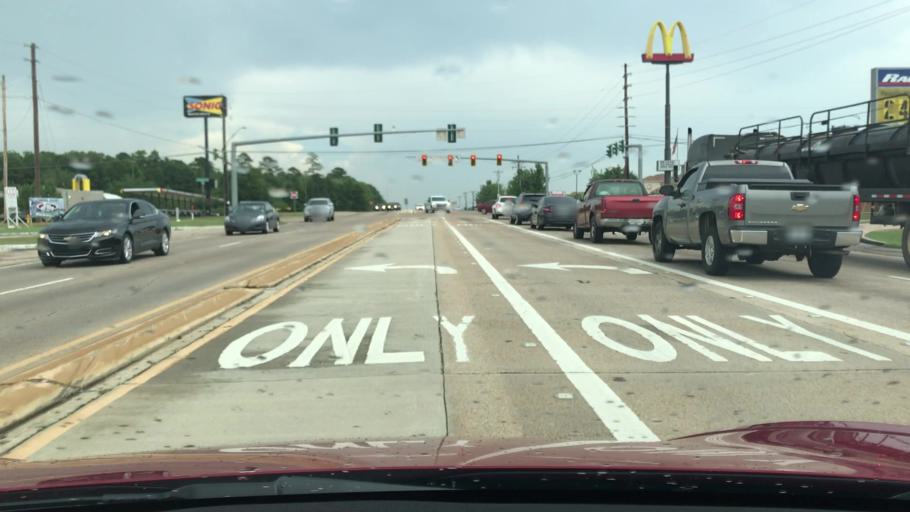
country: US
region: Louisiana
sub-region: Bossier Parish
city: Bossier City
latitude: 32.3983
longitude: -93.7642
